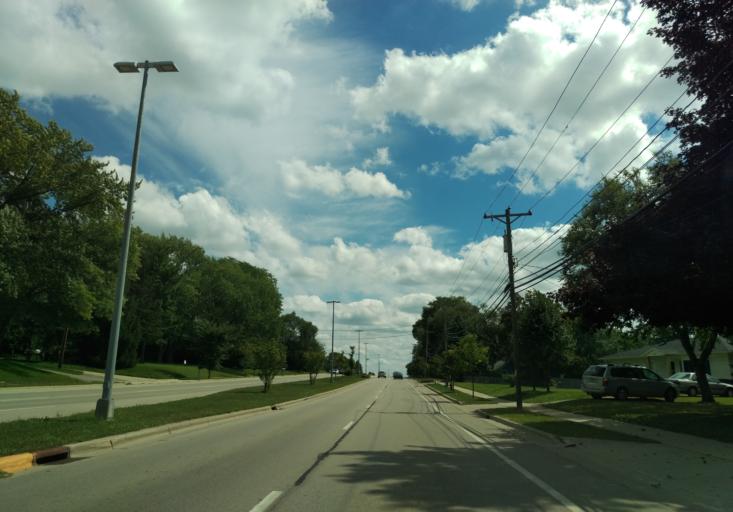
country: US
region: Wisconsin
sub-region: Dane County
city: Maple Bluff
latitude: 43.1371
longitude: -89.3806
